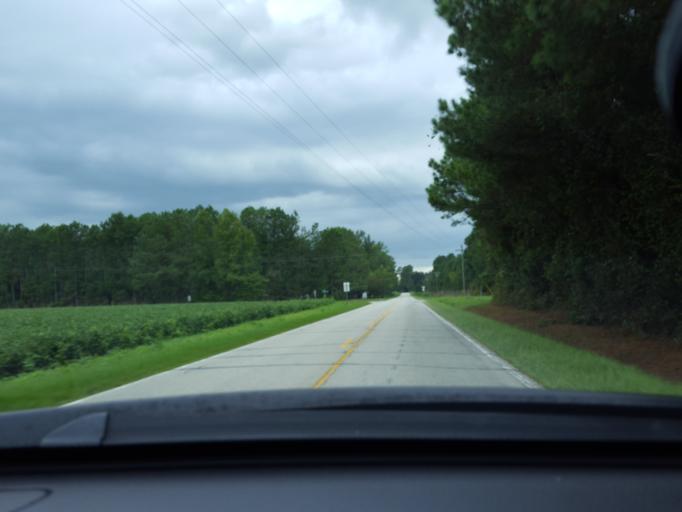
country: US
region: North Carolina
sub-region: Duplin County
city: Rose Hill
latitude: 34.8005
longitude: -78.2358
